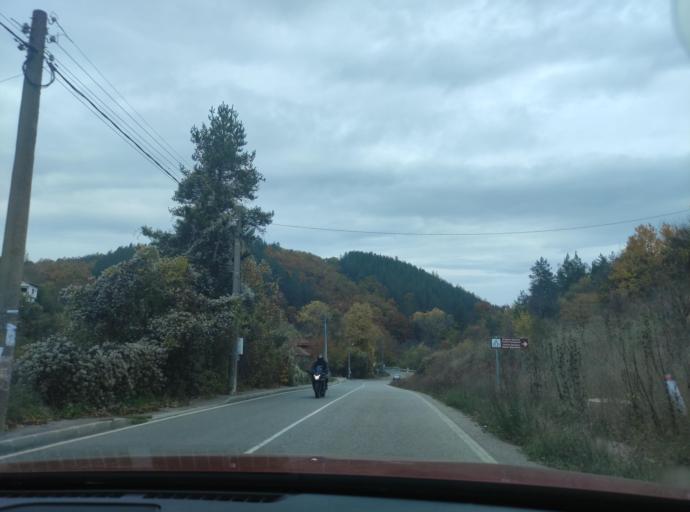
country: BG
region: Sofiya
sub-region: Obshtina Godech
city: Godech
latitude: 42.9742
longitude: 23.1394
